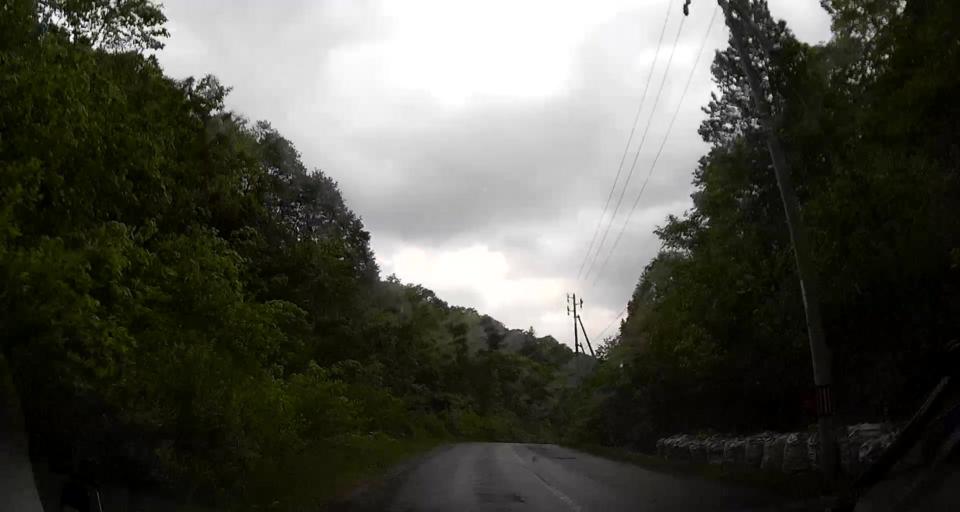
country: JP
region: Hokkaido
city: Otaru
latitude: 42.9159
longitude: 140.9310
